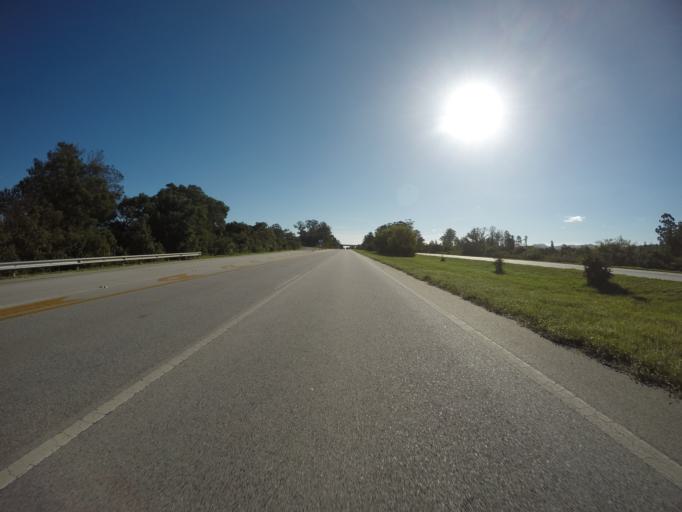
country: ZA
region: Eastern Cape
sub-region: Nelson Mandela Bay Metropolitan Municipality
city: Uitenhage
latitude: -33.9014
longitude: 25.1753
